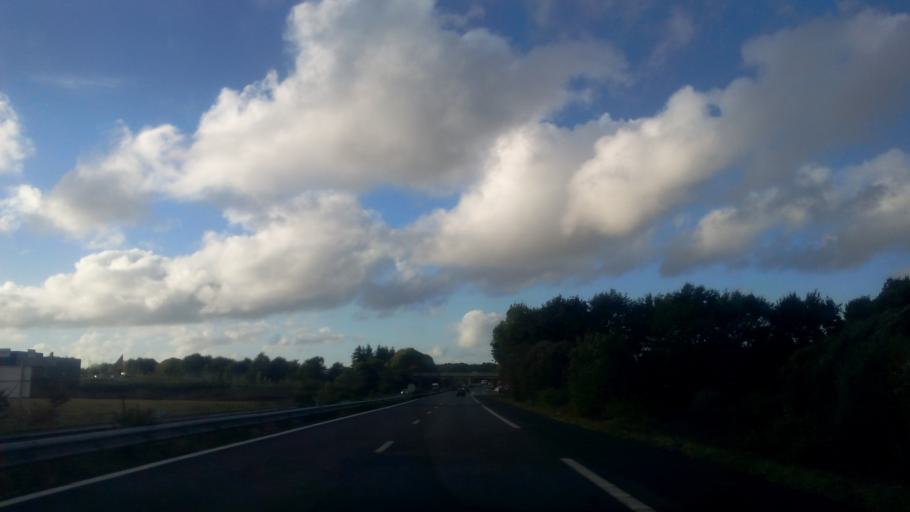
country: FR
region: Pays de la Loire
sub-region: Departement de la Loire-Atlantique
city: Pontchateau
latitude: 47.4355
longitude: -2.0703
